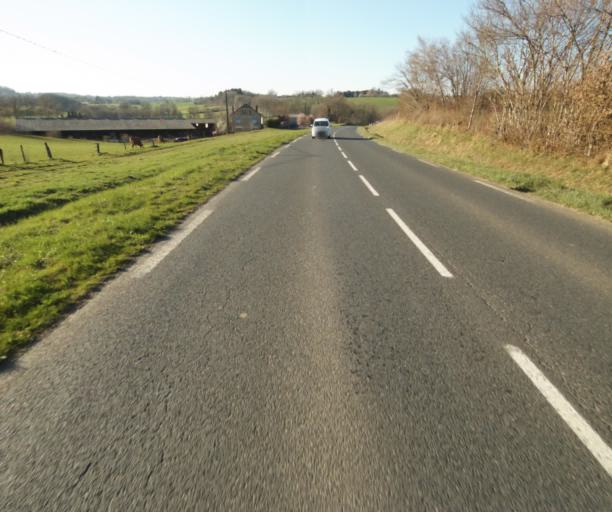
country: FR
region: Limousin
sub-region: Departement de la Correze
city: Chamboulive
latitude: 45.4140
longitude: 1.7149
